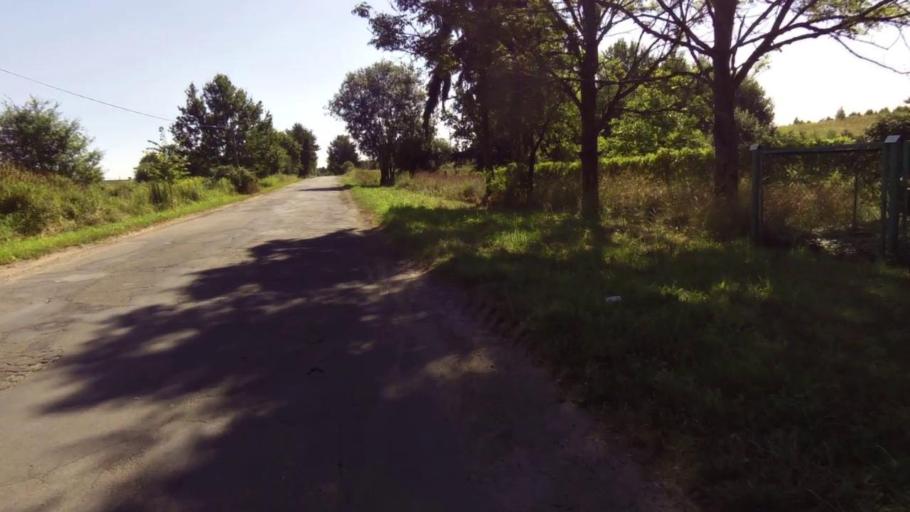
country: PL
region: West Pomeranian Voivodeship
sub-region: Powiat drawski
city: Zlocieniec
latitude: 53.5247
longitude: 16.0246
